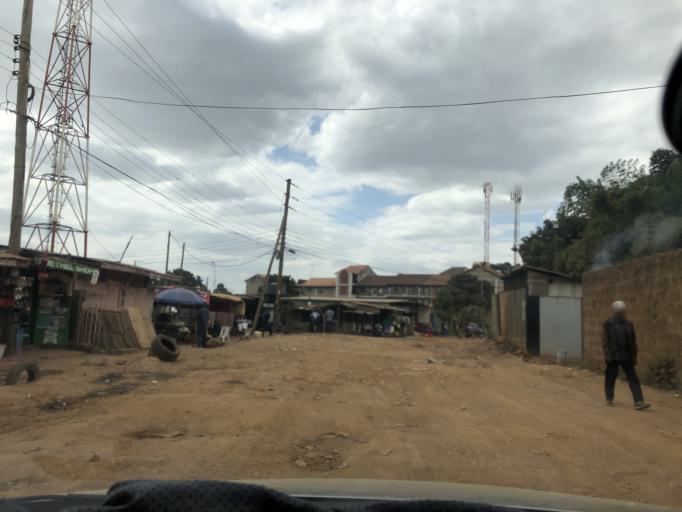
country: KE
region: Nairobi Area
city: Pumwani
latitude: -1.2304
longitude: 36.8770
